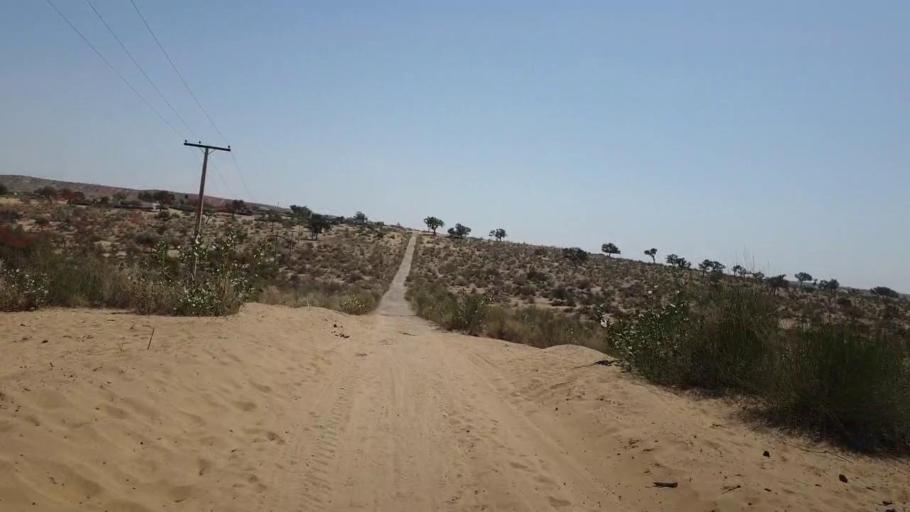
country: PK
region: Sindh
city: Nabisar
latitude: 25.1079
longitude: 69.9012
